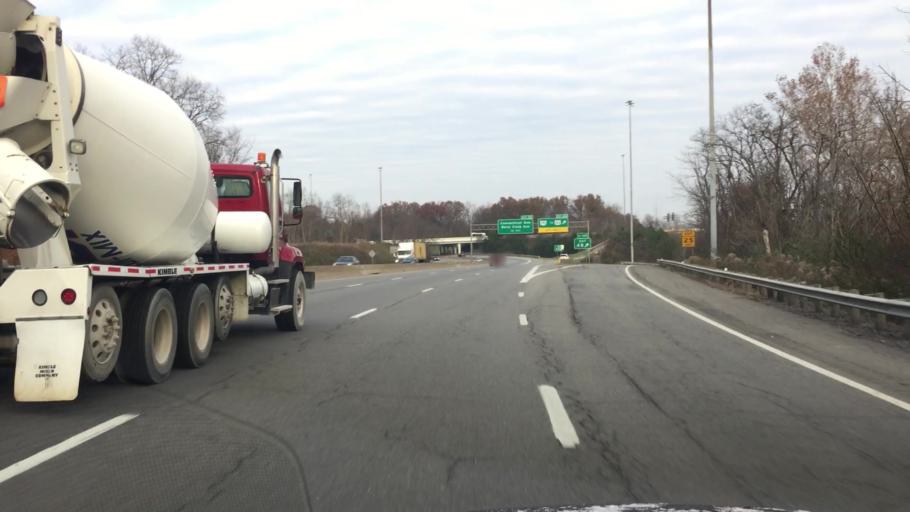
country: US
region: Ohio
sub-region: Mahoning County
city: Youngstown
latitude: 41.1019
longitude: -80.6750
